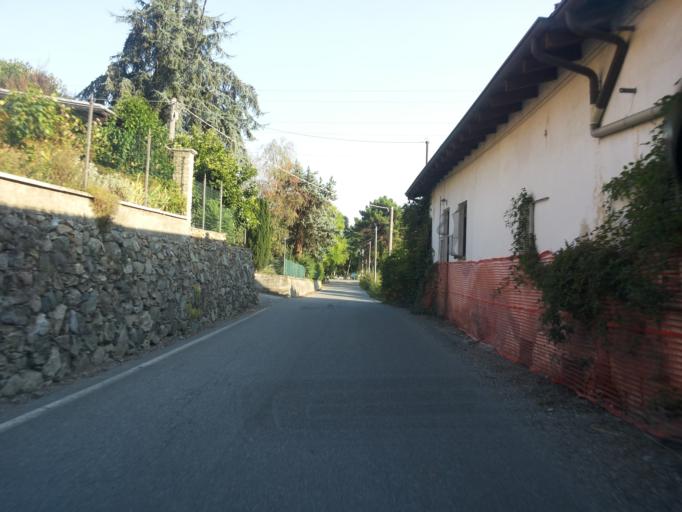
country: IT
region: Piedmont
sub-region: Provincia di Biella
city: Zimone
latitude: 45.4331
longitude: 8.0309
